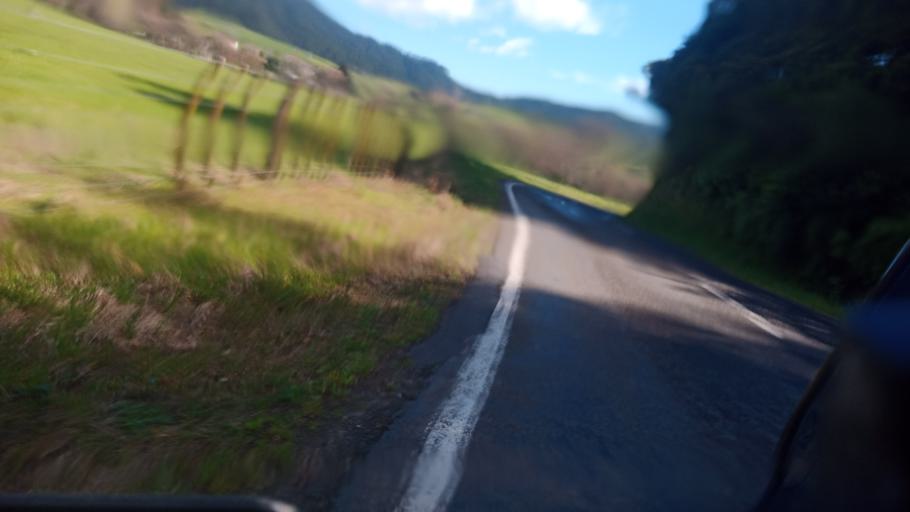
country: NZ
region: Bay of Plenty
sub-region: Opotiki District
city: Opotiki
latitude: -38.0139
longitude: 177.4006
